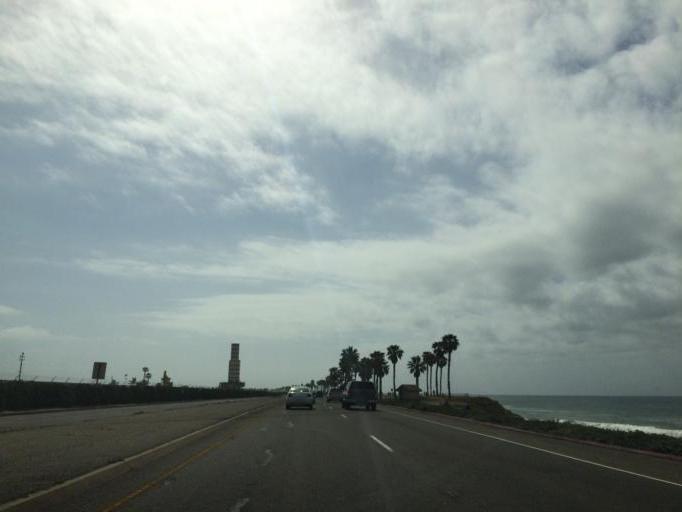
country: US
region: California
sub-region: Orange County
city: Huntington Beach
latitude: 33.6767
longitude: -118.0283
